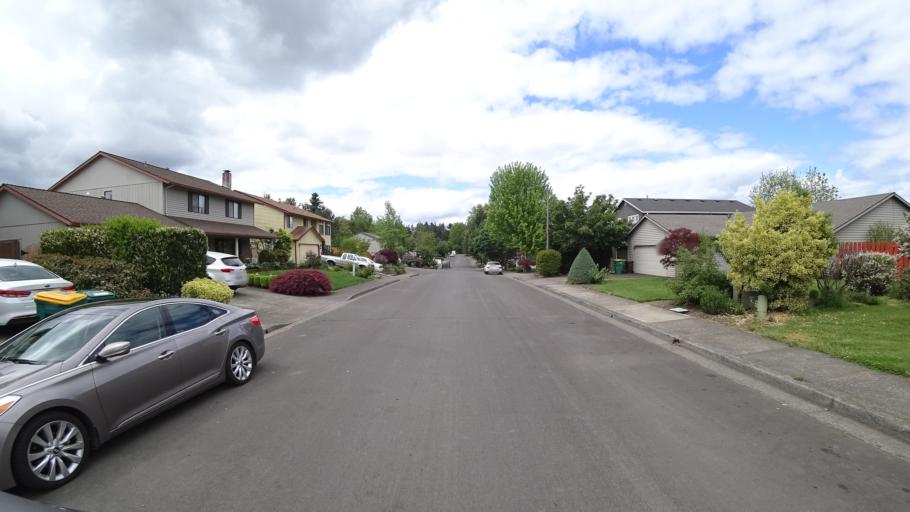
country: US
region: Oregon
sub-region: Washington County
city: Aloha
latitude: 45.4653
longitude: -122.8533
